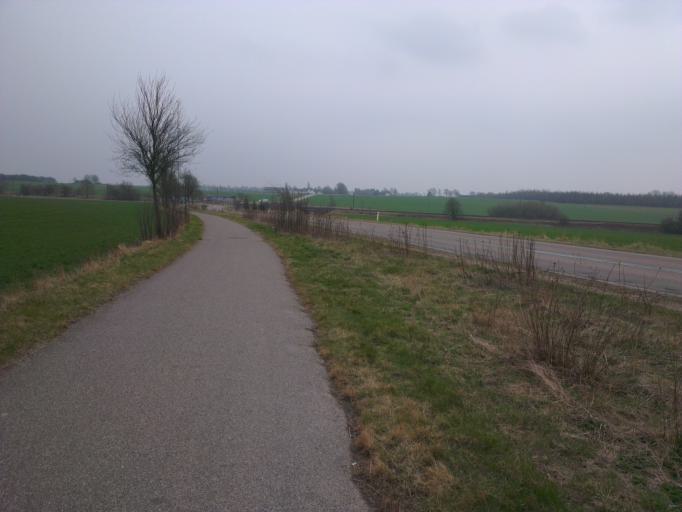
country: DK
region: Capital Region
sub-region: Frederikssund Kommune
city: Frederikssund
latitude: 55.8128
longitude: 12.1059
